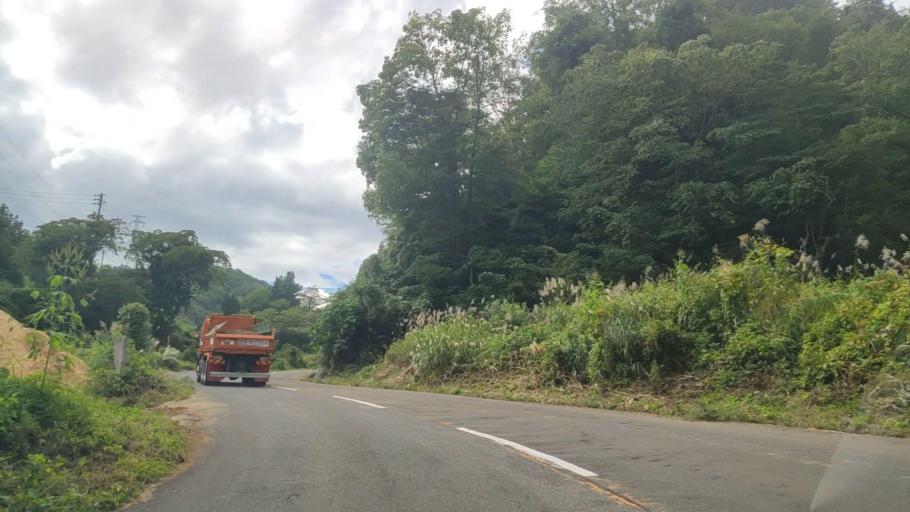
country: JP
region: Nagano
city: Iiyama
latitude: 36.8897
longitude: 138.3230
